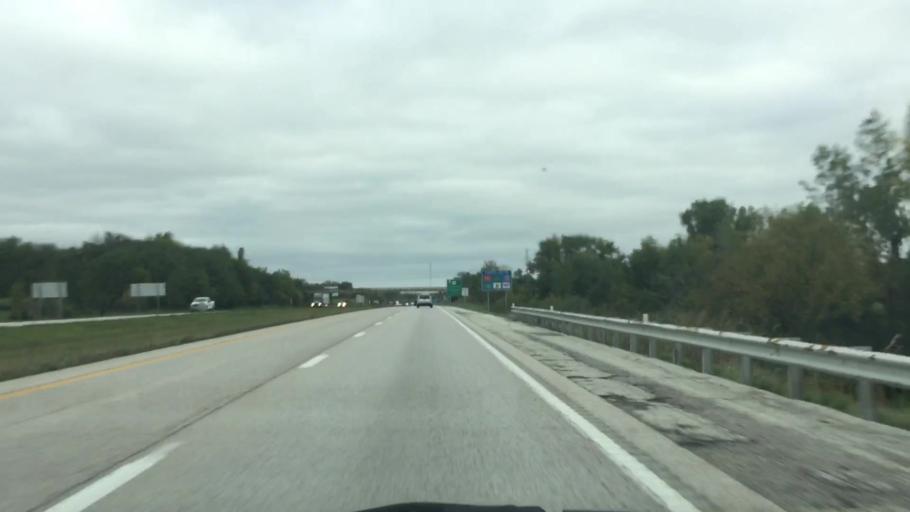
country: US
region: Missouri
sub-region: Clinton County
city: Cameron
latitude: 39.7395
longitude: -94.2202
